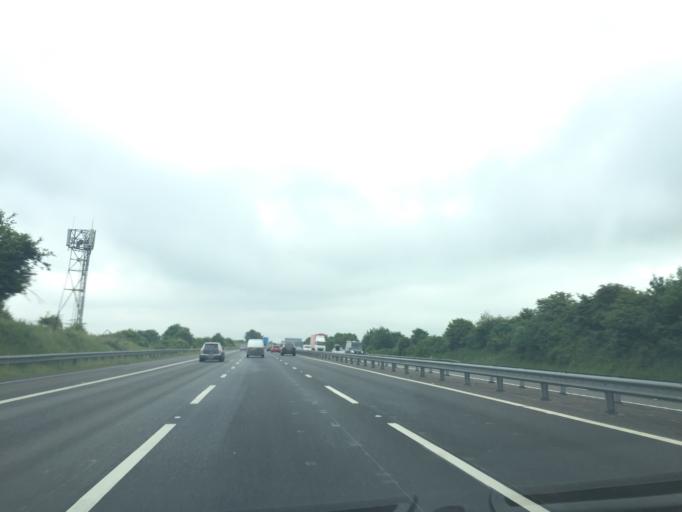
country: GB
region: England
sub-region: Hampshire
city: Overton
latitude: 51.2120
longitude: -1.1732
